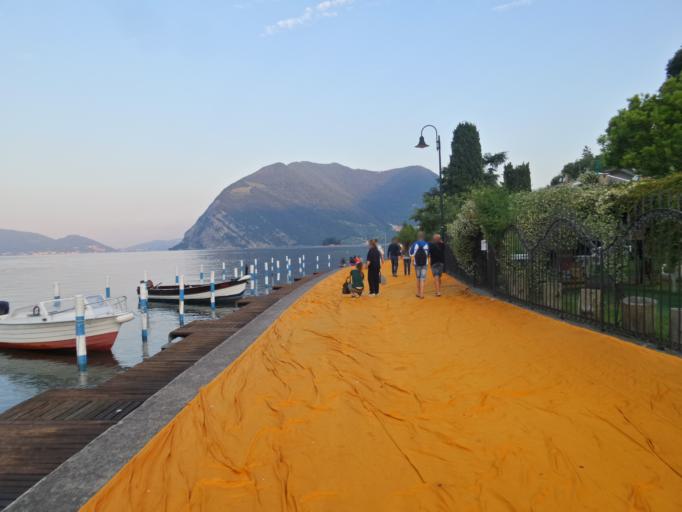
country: IT
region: Lombardy
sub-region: Provincia di Brescia
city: Sulzano
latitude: 45.6928
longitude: 10.0911
